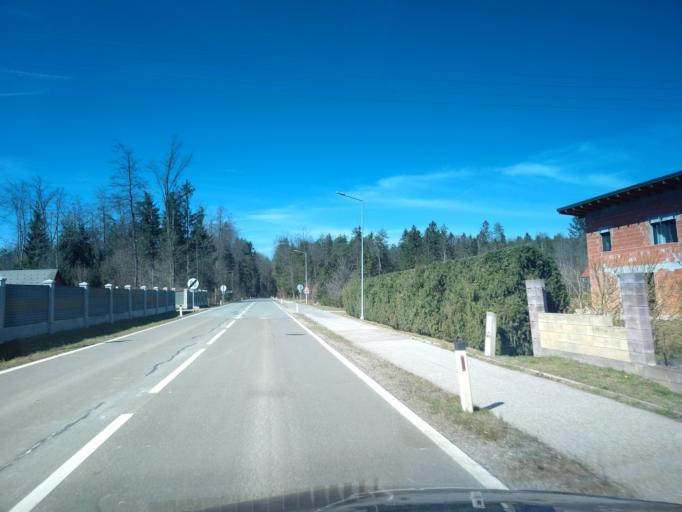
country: AT
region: Styria
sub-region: Politischer Bezirk Deutschlandsberg
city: Sankt Peter im Sulmtal
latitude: 46.7702
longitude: 15.2608
